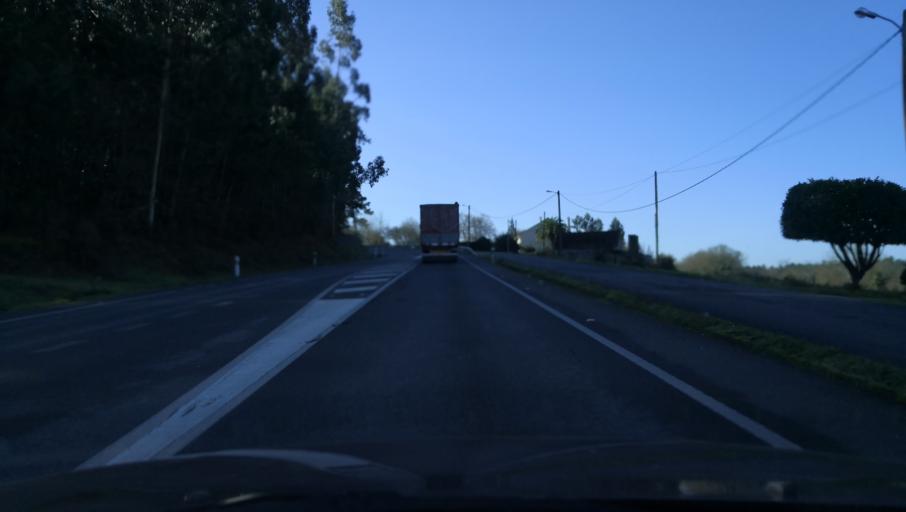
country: ES
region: Galicia
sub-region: Provincia da Coruna
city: Vedra
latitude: 42.8023
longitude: -8.4770
